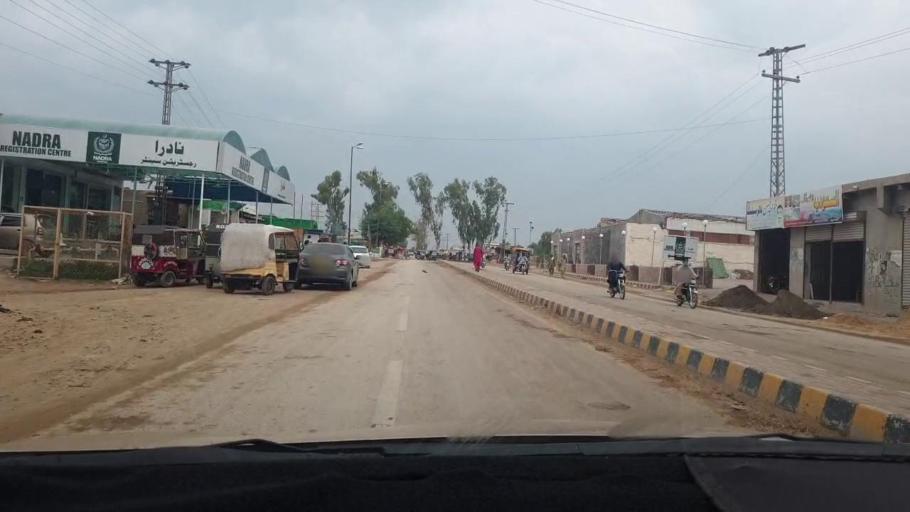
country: PK
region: Sindh
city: Larkana
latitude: 27.5772
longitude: 68.2253
